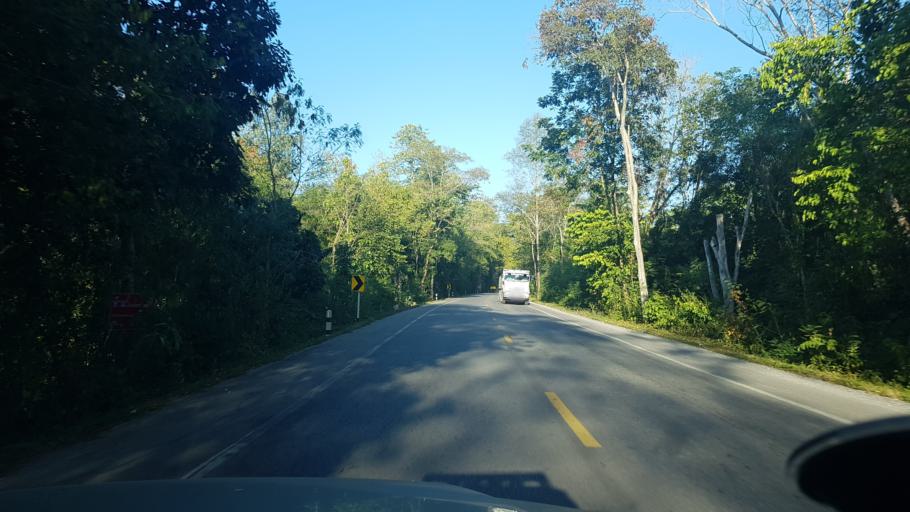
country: TH
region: Khon Kaen
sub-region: Amphoe Phu Pha Man
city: Phu Pha Man
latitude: 16.6311
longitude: 101.8367
